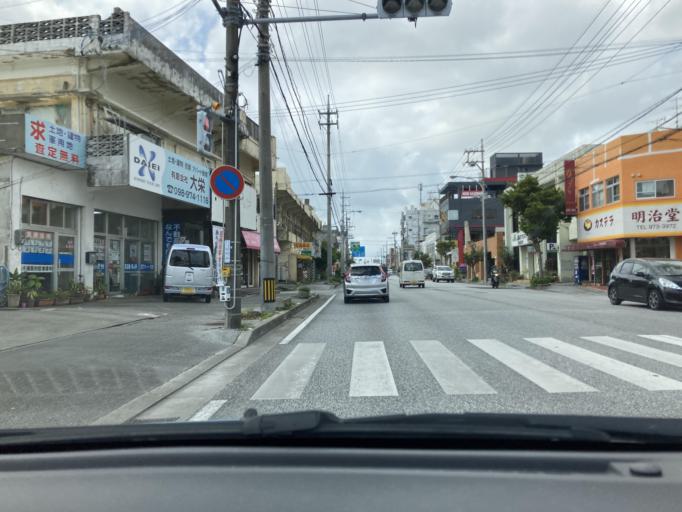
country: JP
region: Okinawa
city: Gushikawa
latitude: 26.3563
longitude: 127.8338
